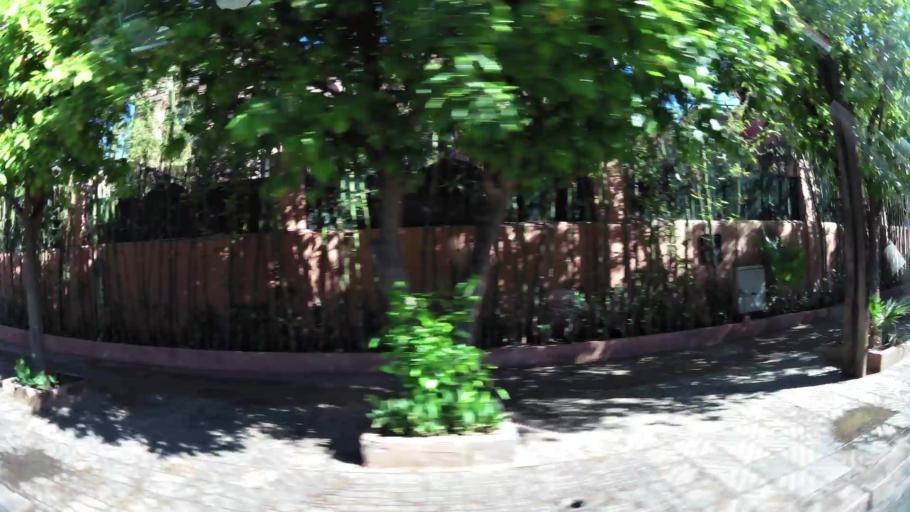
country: MA
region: Marrakech-Tensift-Al Haouz
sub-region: Marrakech
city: Marrakesh
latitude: 31.6428
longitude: -8.0149
